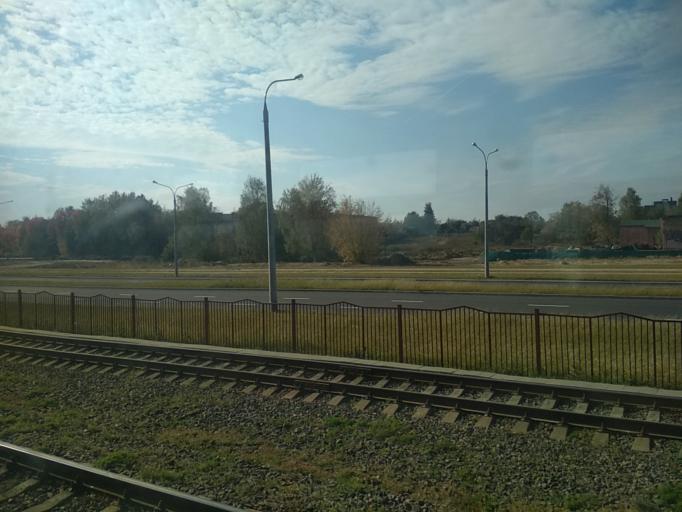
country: BY
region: Minsk
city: Minsk
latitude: 53.8629
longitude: 27.5597
